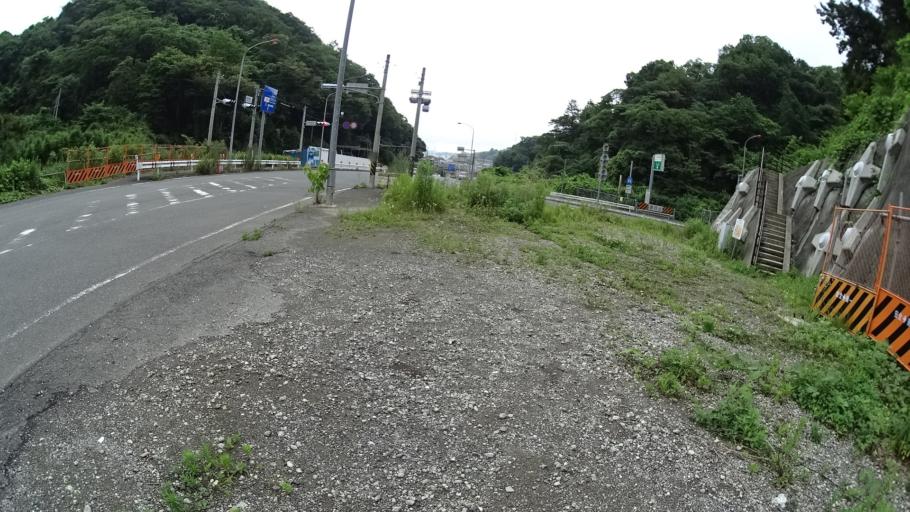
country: JP
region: Kanagawa
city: Yokosuka
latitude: 35.2467
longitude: 139.6574
